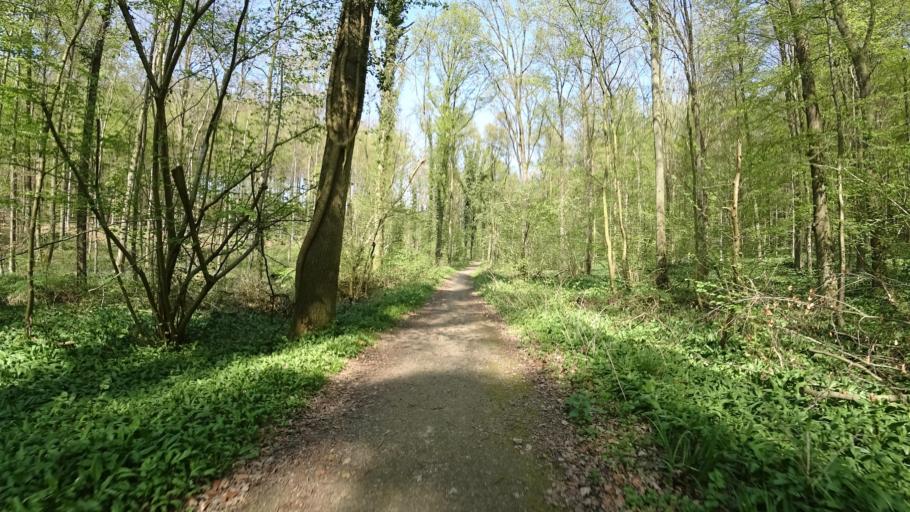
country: BE
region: Wallonia
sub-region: Province du Brabant Wallon
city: Braine-le-Chateau
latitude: 50.7106
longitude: 4.2760
